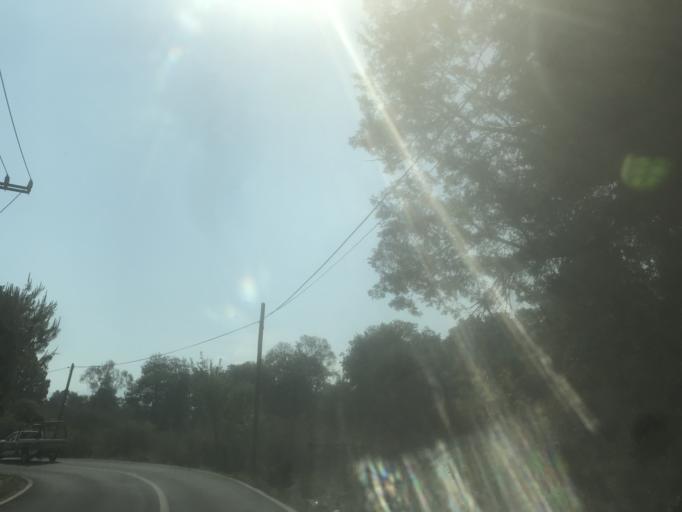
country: MX
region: Mexico
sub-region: Ecatzingo
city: San Marcos Tecomaxusco
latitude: 18.9983
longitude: -98.7729
